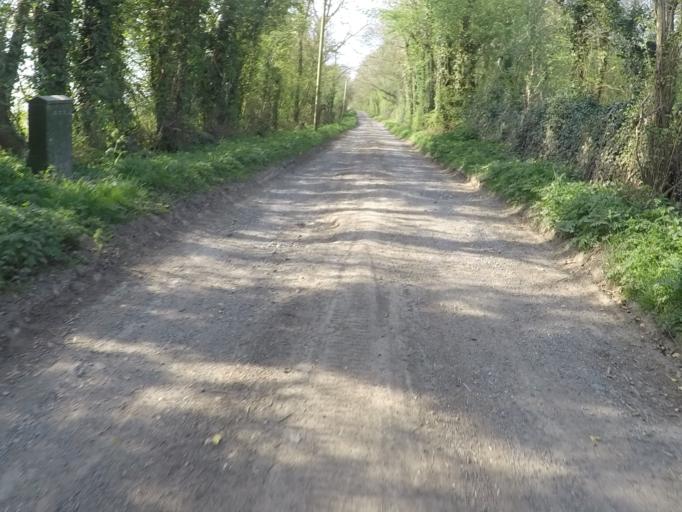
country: GB
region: England
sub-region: Oxfordshire
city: Charlbury
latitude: 51.8896
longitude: -1.4579
